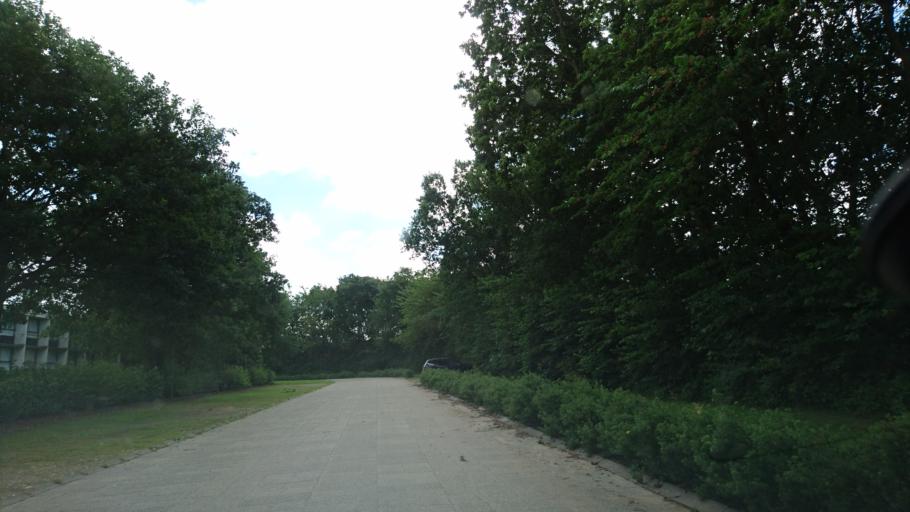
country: DK
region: Central Jutland
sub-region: Arhus Kommune
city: Stavtrup
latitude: 56.1697
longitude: 10.1120
